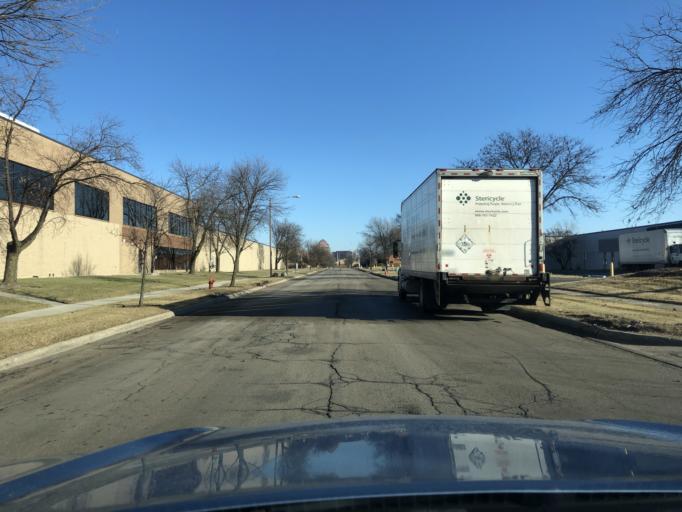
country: US
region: Illinois
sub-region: DuPage County
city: Itasca
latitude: 41.9859
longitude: -88.0392
